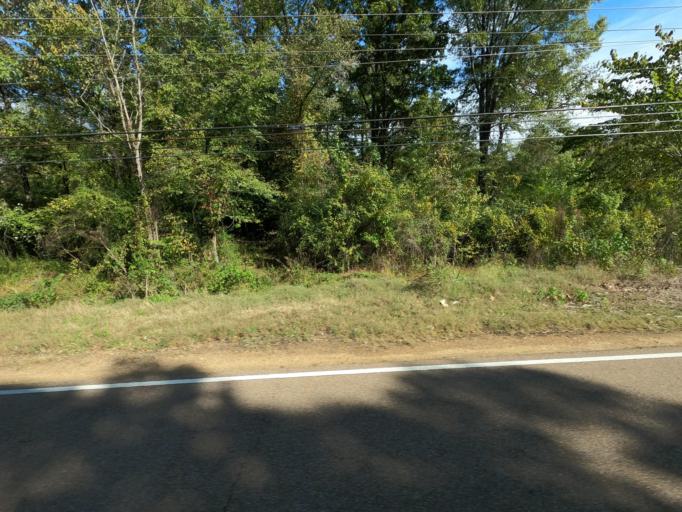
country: US
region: Tennessee
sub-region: Fayette County
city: Hickory Withe
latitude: 35.2227
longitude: -89.6502
